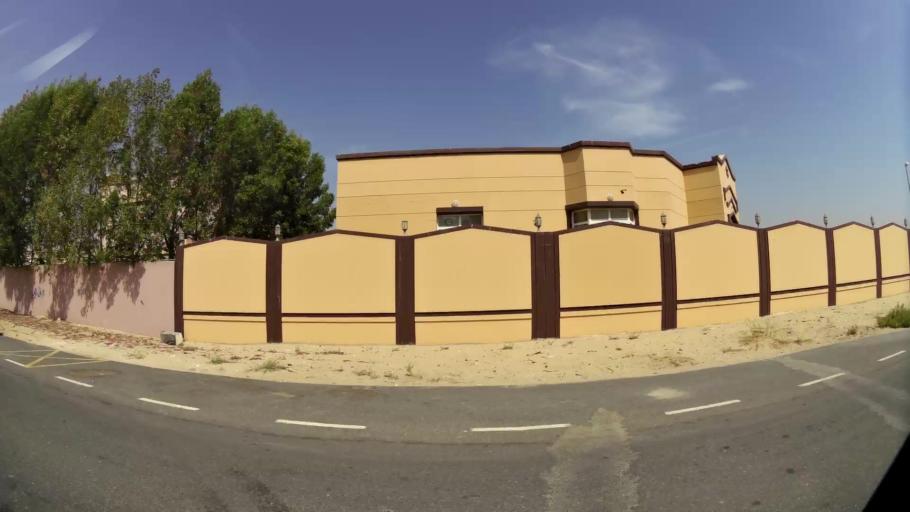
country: AE
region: Ash Shariqah
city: Sharjah
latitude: 25.2061
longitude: 55.4233
